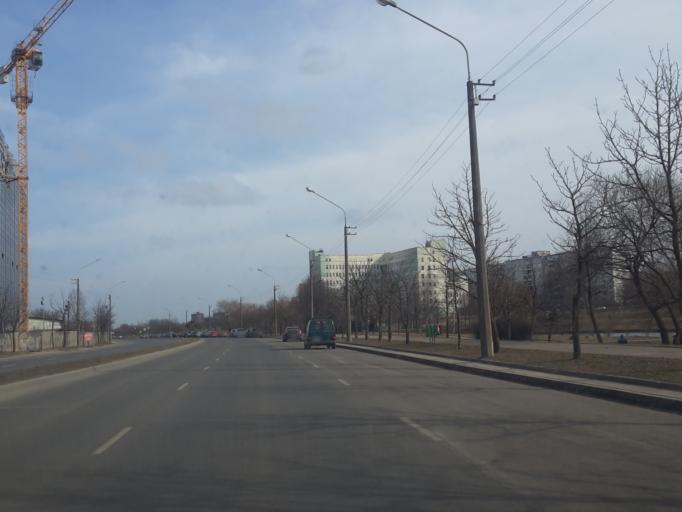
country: BY
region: Minsk
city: Minsk
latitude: 53.9034
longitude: 27.6056
